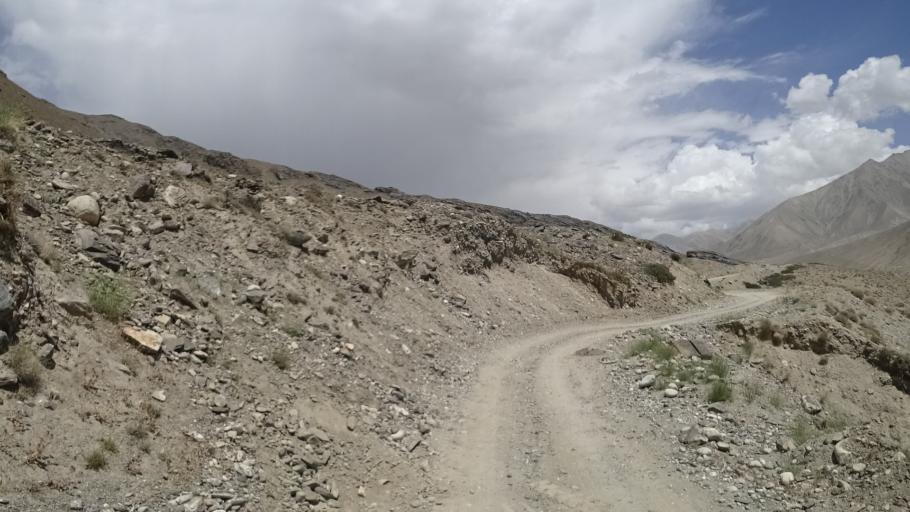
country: AF
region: Badakhshan
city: Khandud
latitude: 37.0951
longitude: 72.7074
